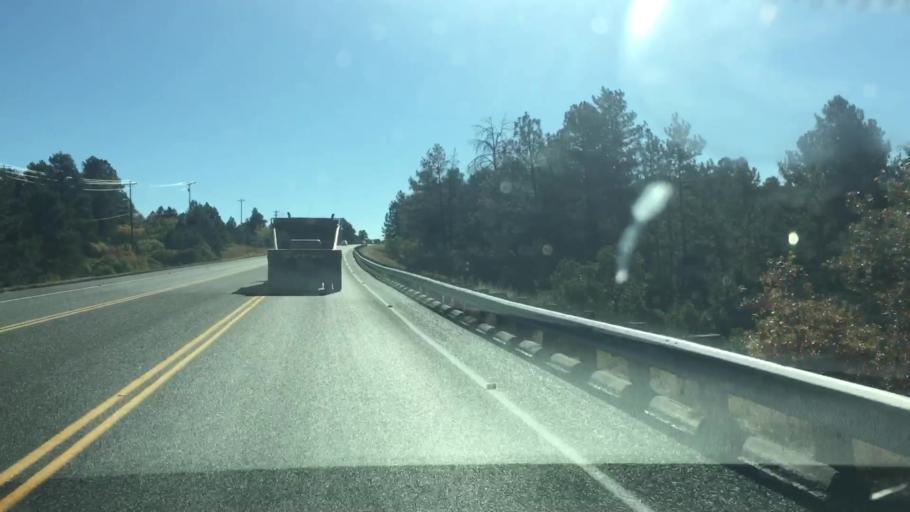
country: US
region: Colorado
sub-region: Elbert County
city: Ponderosa Park
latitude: 39.3763
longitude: -104.6930
